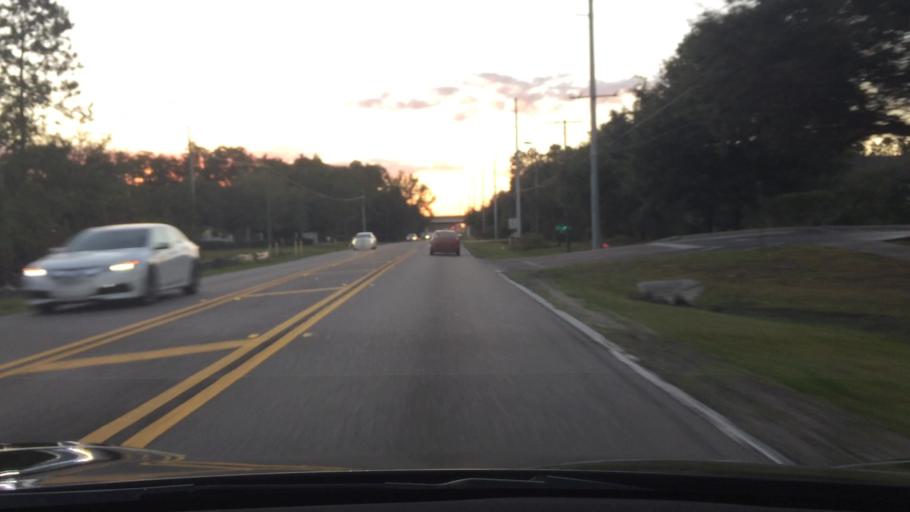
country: US
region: Florida
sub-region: Hillsborough County
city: Greater Northdale
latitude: 28.1279
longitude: -82.5258
